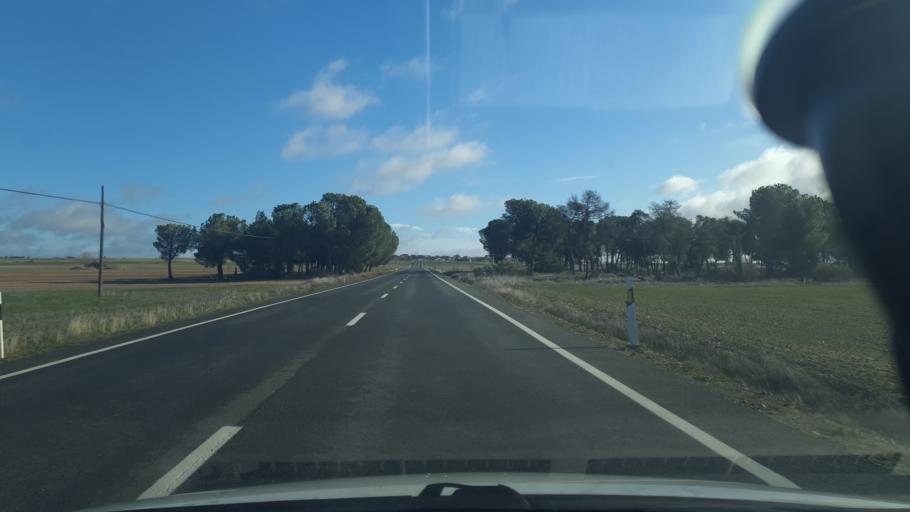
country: ES
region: Castille and Leon
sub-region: Provincia de Segovia
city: Martin Munoz de la Dehesa
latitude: 41.0468
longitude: -4.6479
